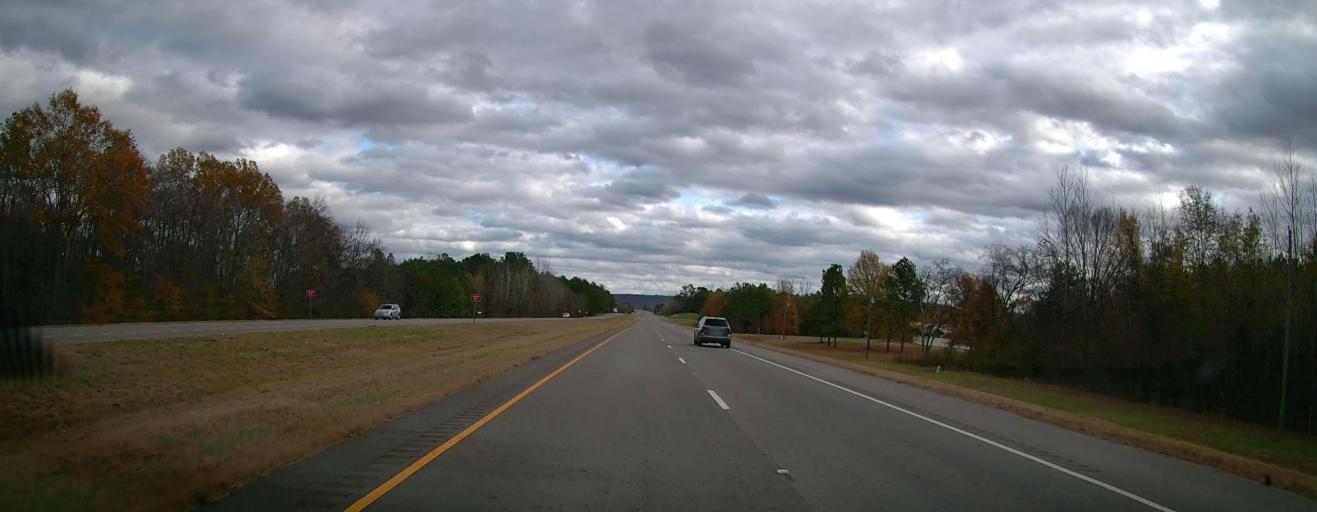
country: US
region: Alabama
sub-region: Morgan County
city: Danville
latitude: 34.3558
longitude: -87.0530
